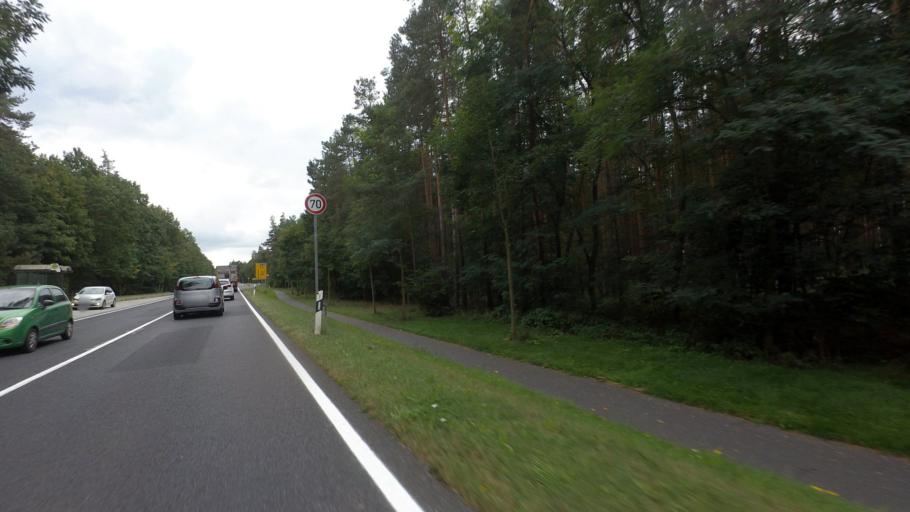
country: DE
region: Saxony
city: Konigswartha
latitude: 51.2935
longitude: 14.3278
